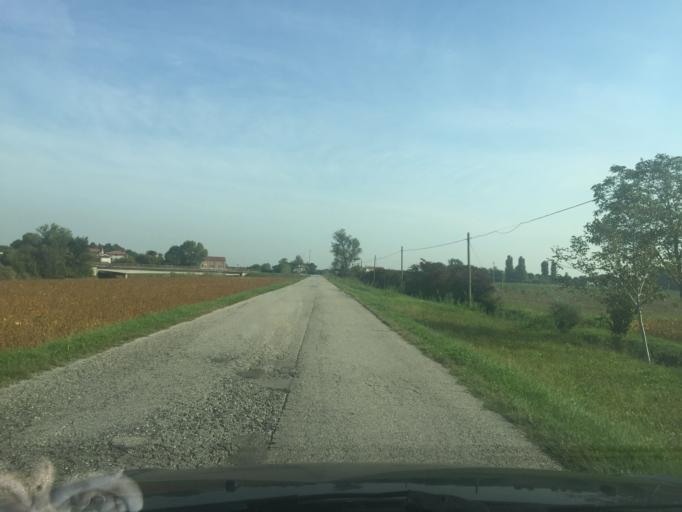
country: IT
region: Veneto
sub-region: Provincia di Venezia
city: Ceggia
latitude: 45.6345
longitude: 12.6549
